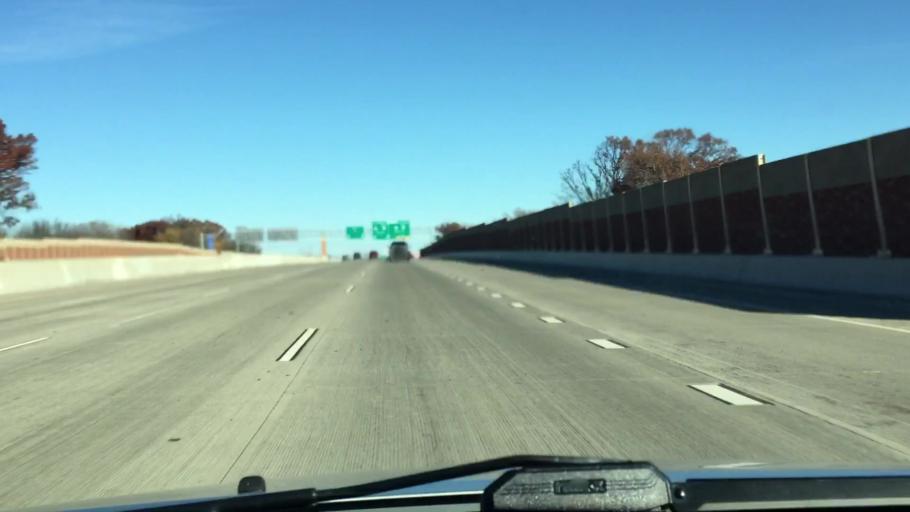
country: US
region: Wisconsin
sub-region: Brown County
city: Howard
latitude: 44.5176
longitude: -88.0822
